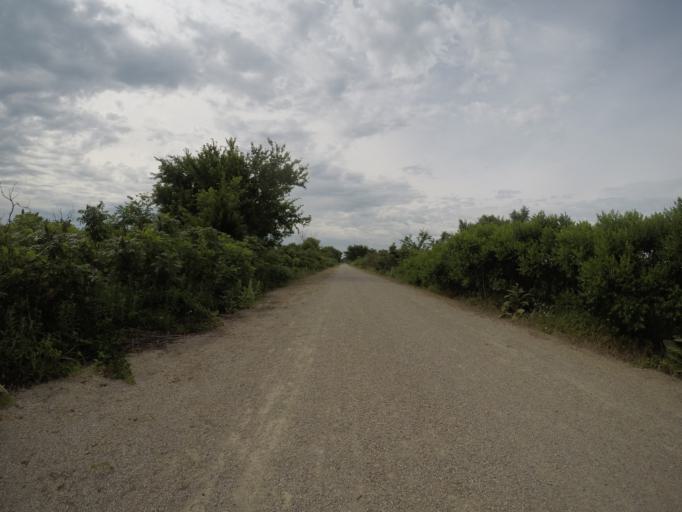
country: US
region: Kansas
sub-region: Anderson County
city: Garnett
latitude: 38.4257
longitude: -95.2632
